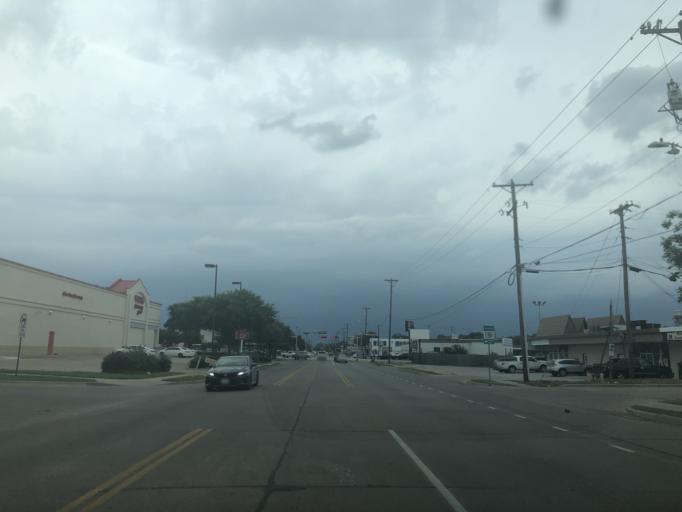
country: US
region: Texas
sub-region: Dallas County
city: Irving
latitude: 32.8102
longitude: -96.9345
